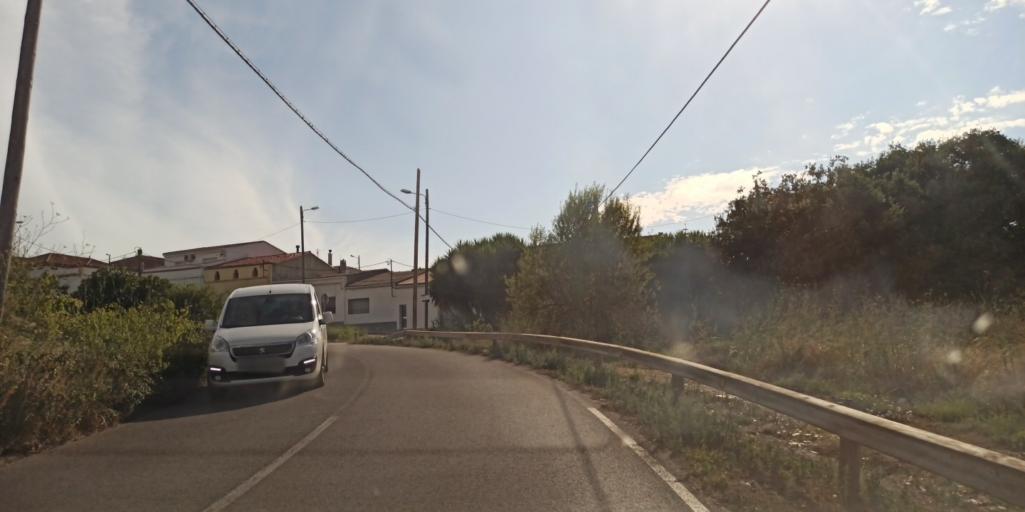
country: ES
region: Catalonia
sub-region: Provincia de Barcelona
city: Santa Coloma de Cervello
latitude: 41.3593
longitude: 2.0237
